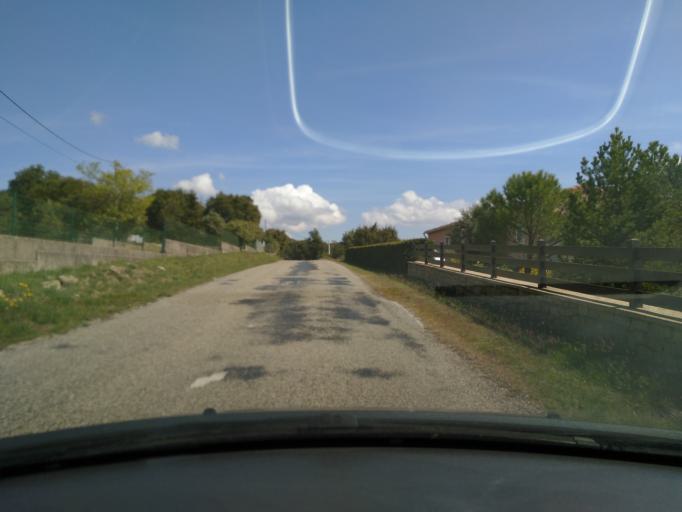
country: FR
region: Rhone-Alpes
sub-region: Departement de l'Ardeche
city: Ruoms
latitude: 44.4495
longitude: 4.3883
